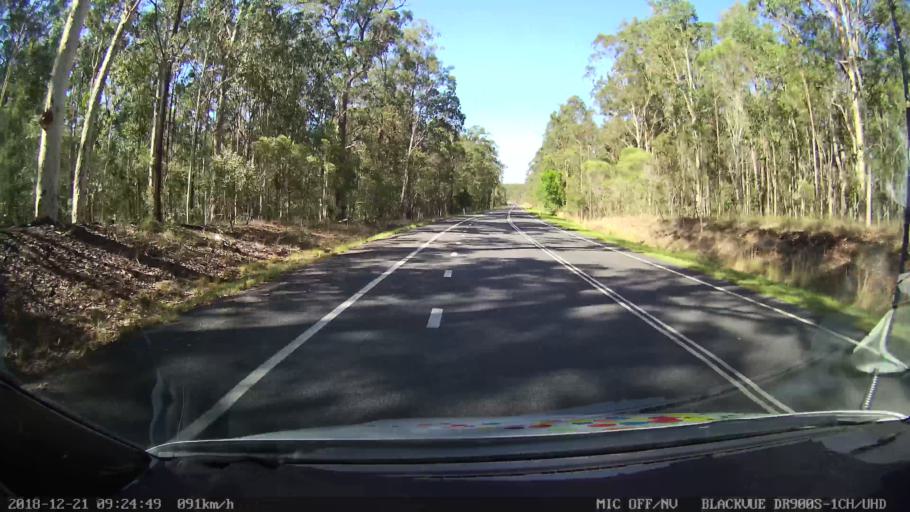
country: AU
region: New South Wales
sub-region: Clarence Valley
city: Maclean
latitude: -29.3723
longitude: 153.0145
